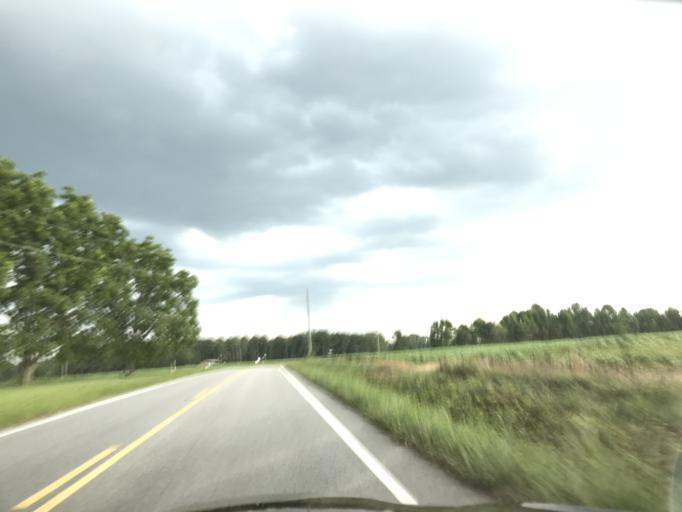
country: US
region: North Carolina
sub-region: Johnston County
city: Four Oaks
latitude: 35.5229
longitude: -78.4653
